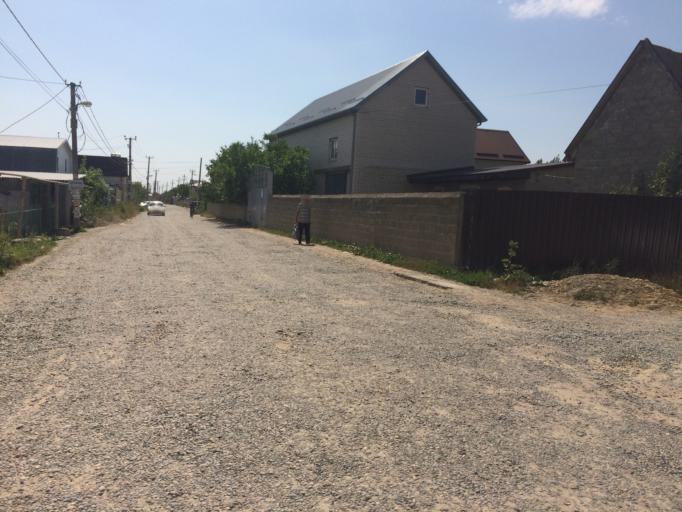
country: RU
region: Stavropol'skiy
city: Tatarka
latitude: 44.9881
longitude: 41.9392
